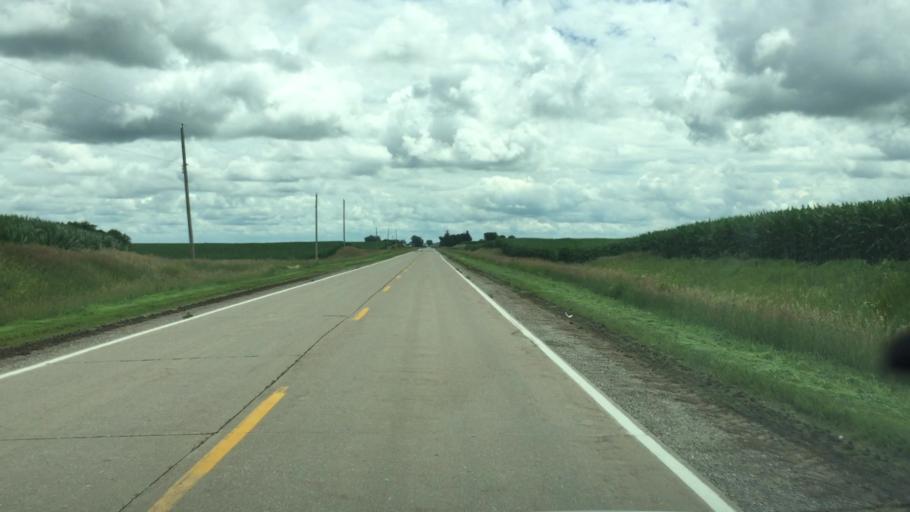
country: US
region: Iowa
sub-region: Jasper County
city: Monroe
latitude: 41.5807
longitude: -93.1316
